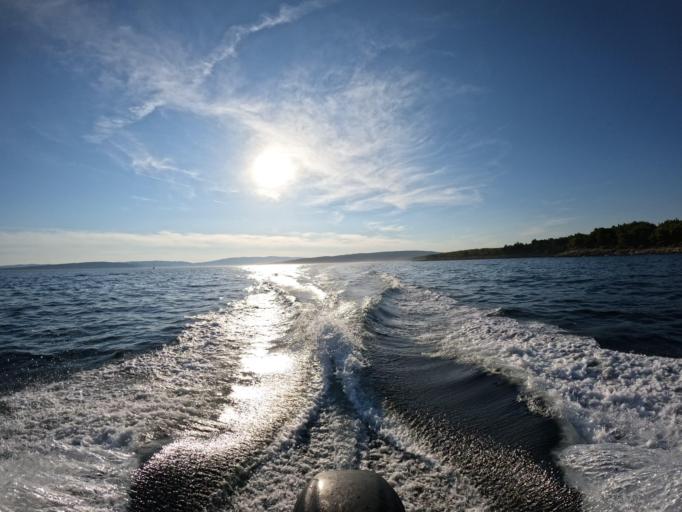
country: HR
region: Primorsko-Goranska
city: Punat
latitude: 45.0130
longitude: 14.6120
